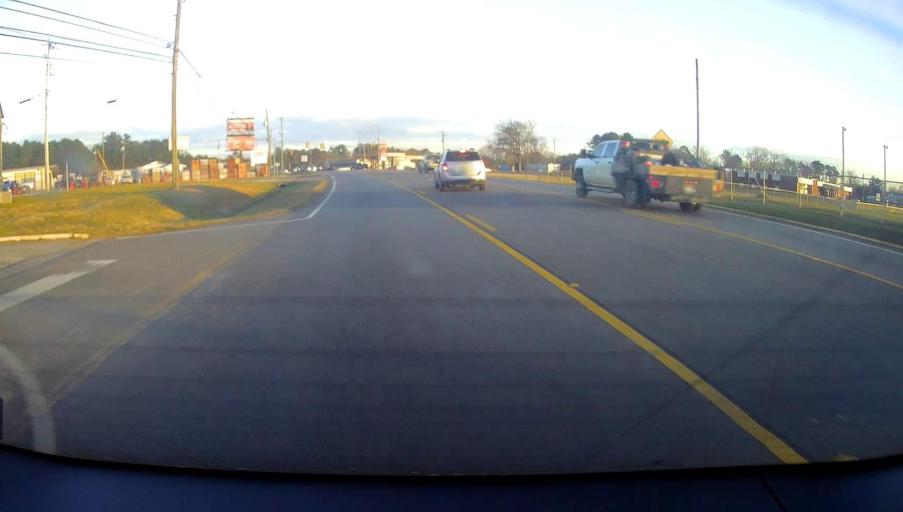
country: US
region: Alabama
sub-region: Etowah County
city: Attalla
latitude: 33.9980
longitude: -86.1057
